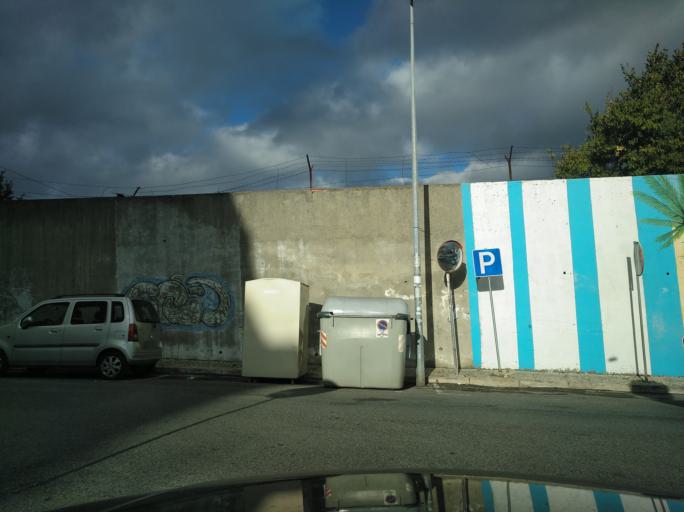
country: PT
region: Lisbon
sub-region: Loures
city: Sacavem
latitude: 38.7954
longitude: -9.1086
